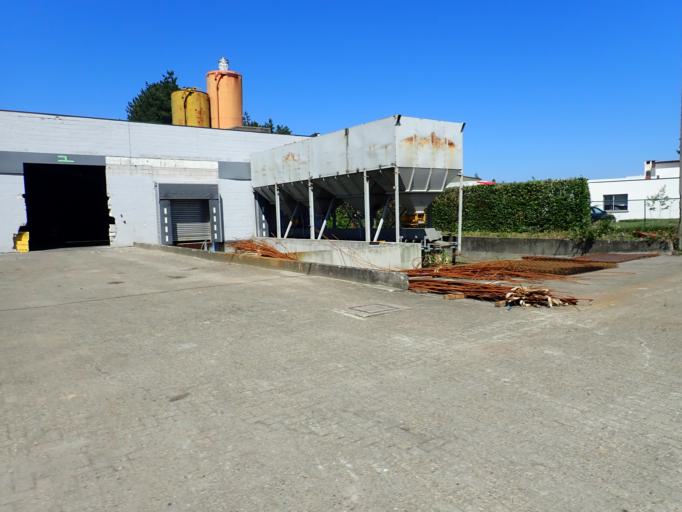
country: BE
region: Flanders
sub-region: Provincie Antwerpen
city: Beerse
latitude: 51.3027
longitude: 4.8419
